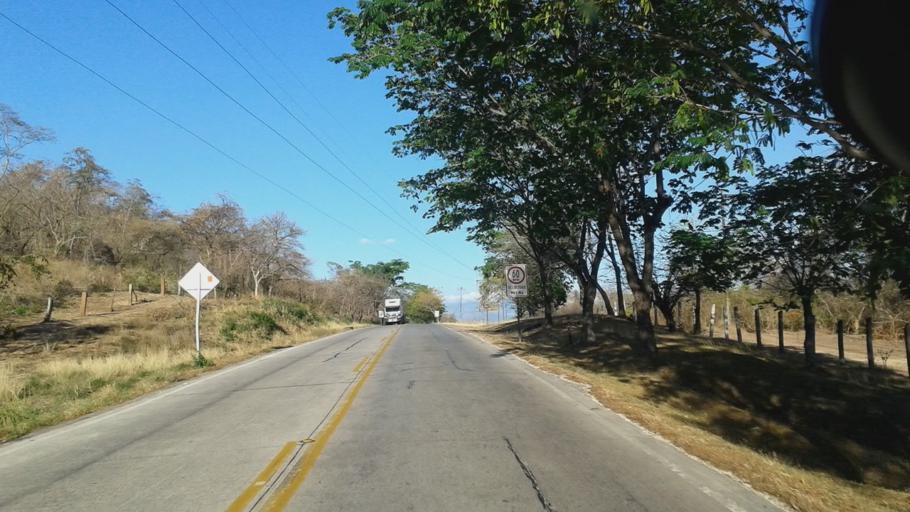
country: CR
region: Guanacaste
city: Nandayure
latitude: 10.2249
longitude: -85.1813
